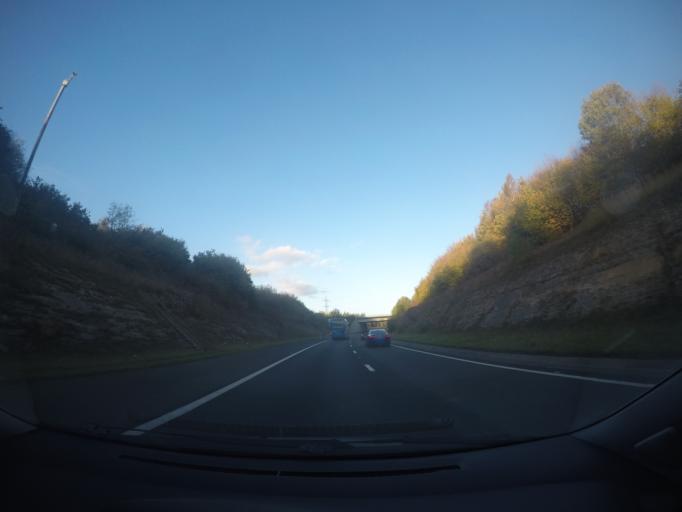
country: GB
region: England
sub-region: City and Borough of Leeds
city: Aberford
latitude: 53.8544
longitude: -1.3425
